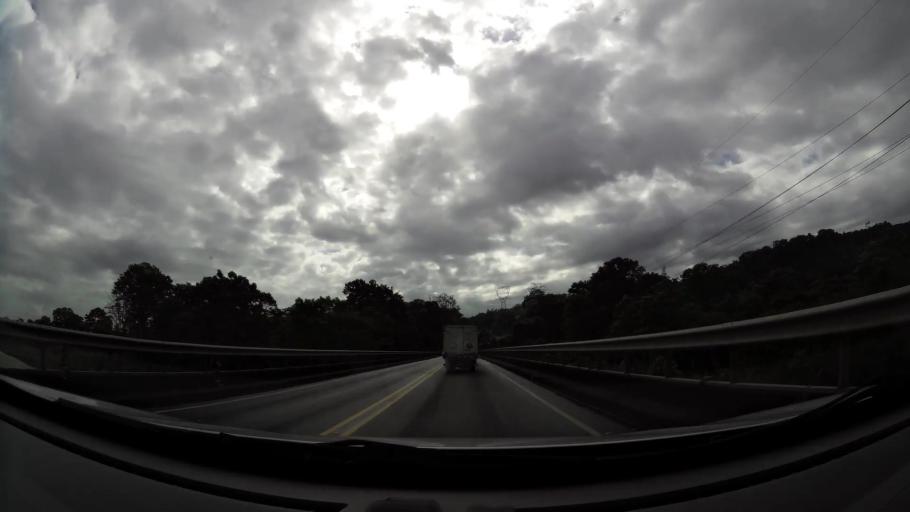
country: CR
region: Limon
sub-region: Canton de Siquirres
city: Siquirres
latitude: 10.1066
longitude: -83.5317
